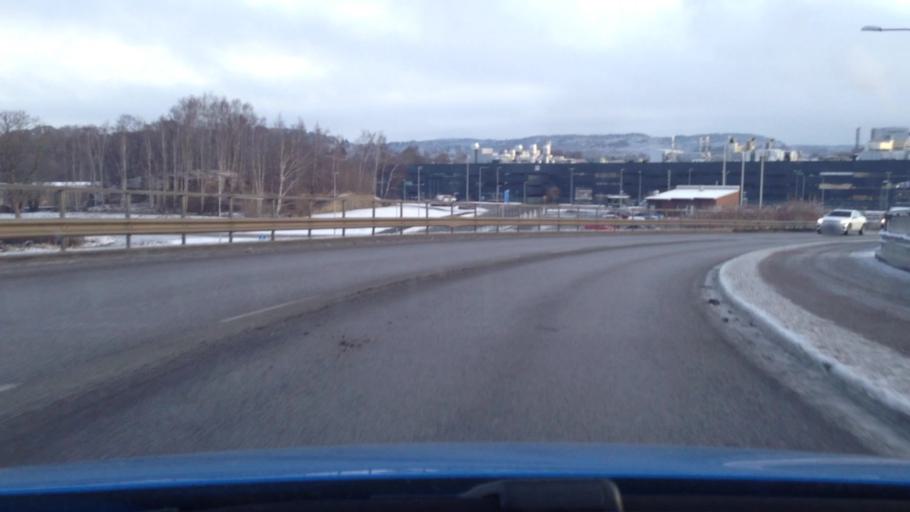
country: SE
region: Vaestra Goetaland
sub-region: Goteborg
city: Eriksbo
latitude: 57.7265
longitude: 12.0236
